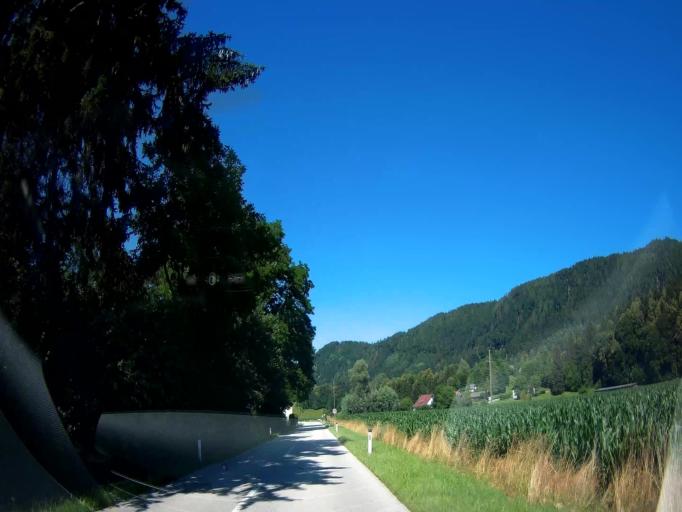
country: AT
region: Carinthia
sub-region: Politischer Bezirk Volkermarkt
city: Gallizien
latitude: 46.5867
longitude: 14.5162
